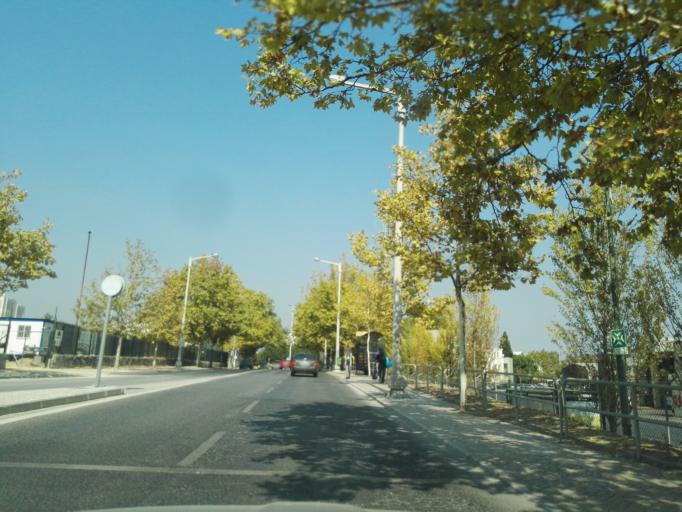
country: PT
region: Lisbon
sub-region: Loures
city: Moscavide
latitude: 38.7568
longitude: -9.1128
